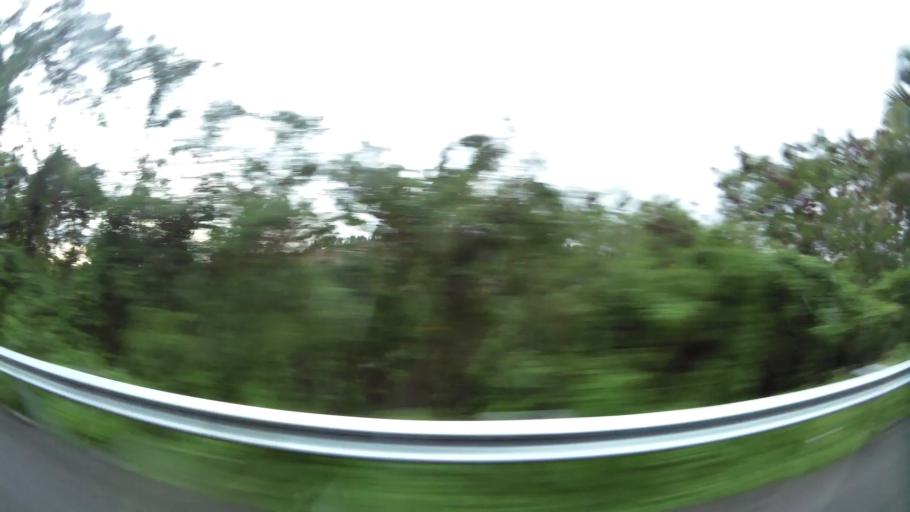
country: DO
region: San Cristobal
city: Villa Altagracia
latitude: 18.6049
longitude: -70.1373
